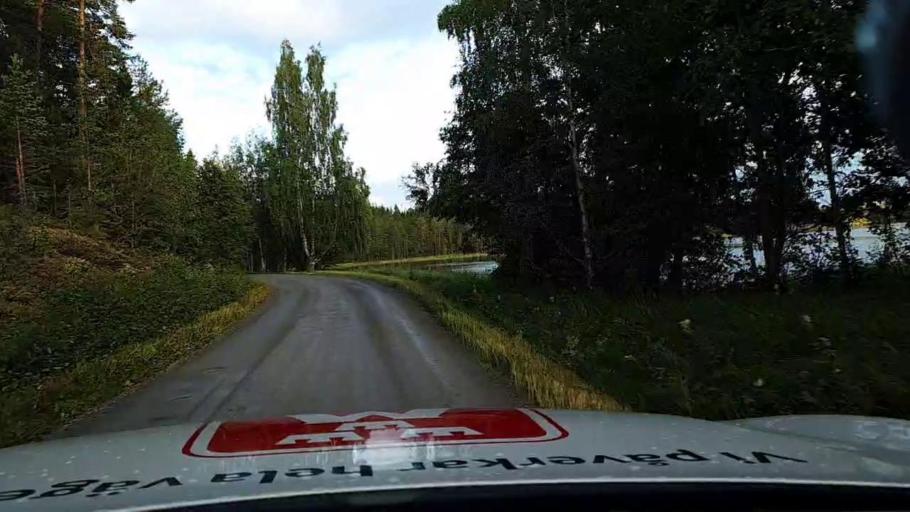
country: SE
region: Jaemtland
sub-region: Bergs Kommun
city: Hoverberg
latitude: 62.8489
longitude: 14.5624
